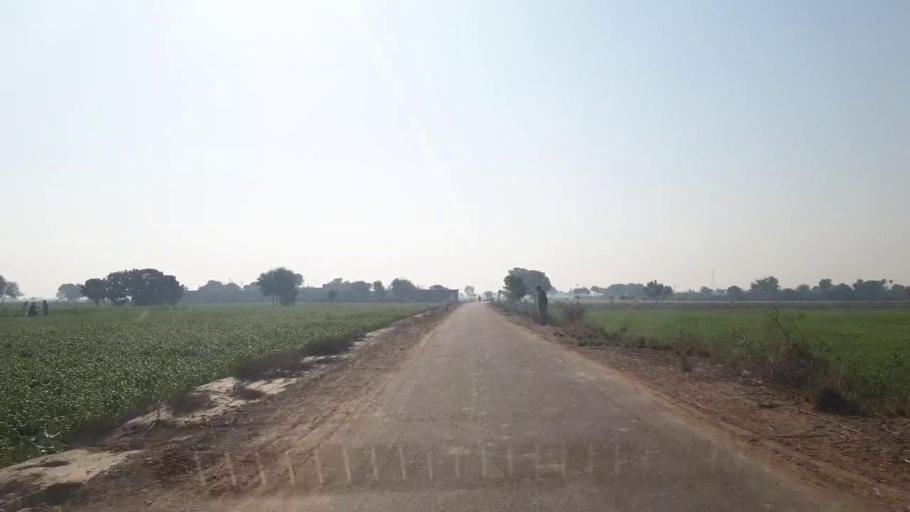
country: PK
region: Sindh
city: Shahpur Chakar
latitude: 26.0749
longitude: 68.5835
